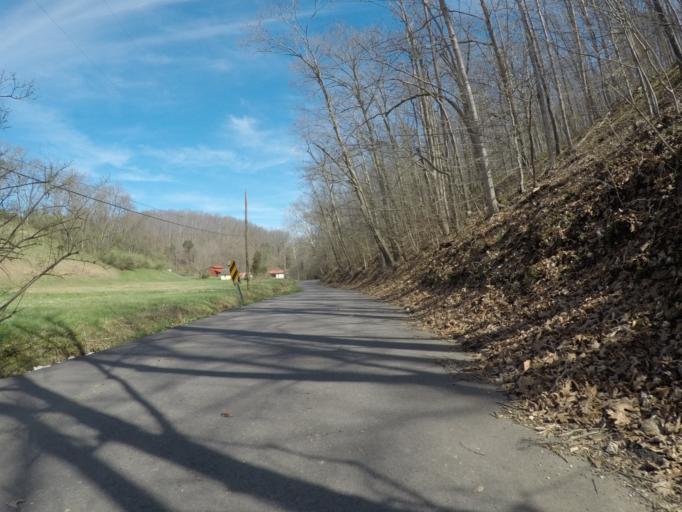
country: US
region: West Virginia
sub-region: Cabell County
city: Pea Ridge
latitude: 38.3968
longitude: -82.3511
